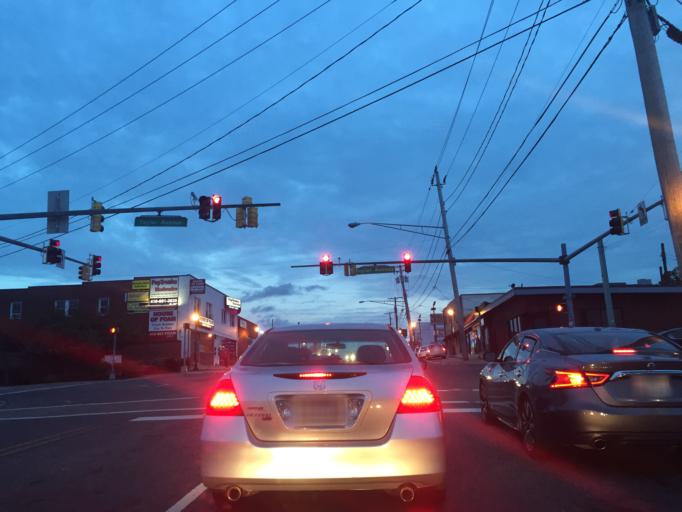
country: US
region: Maryland
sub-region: Baltimore County
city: Parkville
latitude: 39.3741
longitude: -76.5427
